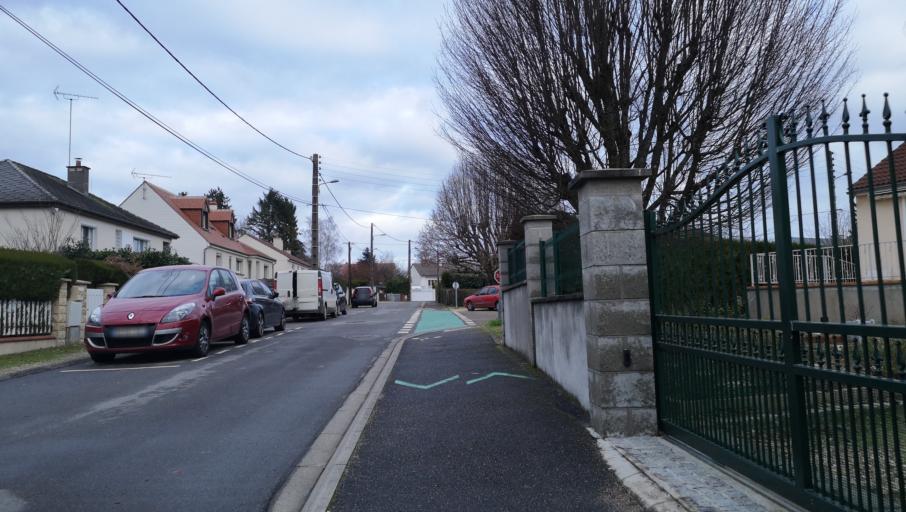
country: FR
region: Centre
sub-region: Departement du Loiret
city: Boigny-sur-Bionne
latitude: 47.9205
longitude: 2.0059
